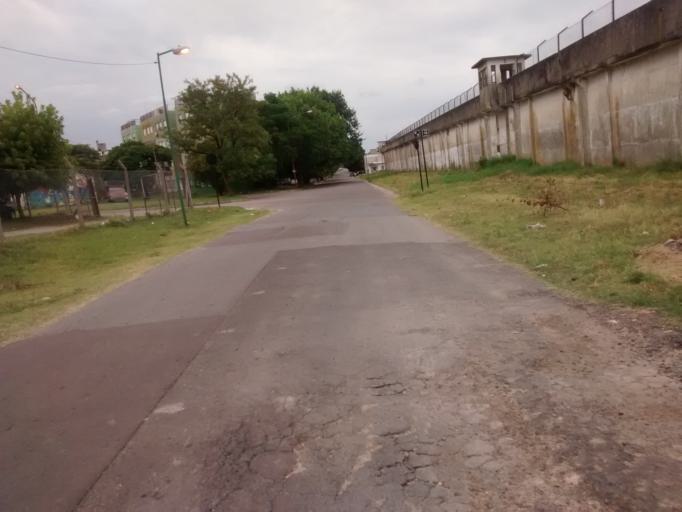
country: AR
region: Buenos Aires
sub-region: Partido de La Plata
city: La Plata
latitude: -34.9380
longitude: -57.9248
